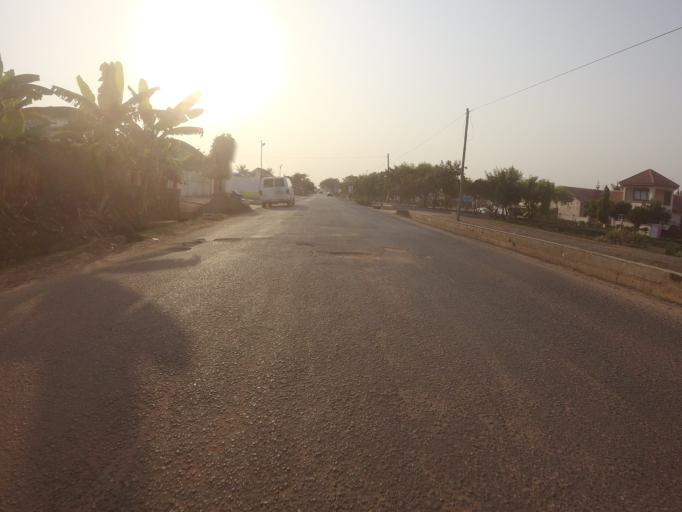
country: GH
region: Greater Accra
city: Nungua
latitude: 5.6166
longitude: -0.0491
